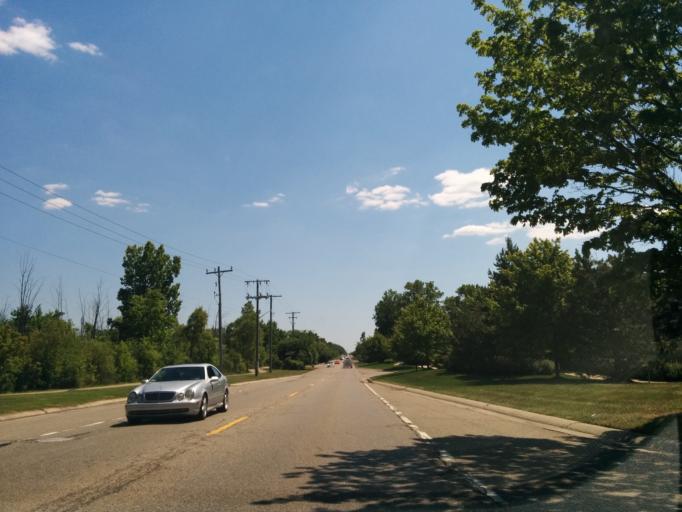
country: US
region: Michigan
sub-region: Oakland County
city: West Bloomfield Township
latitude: 42.5359
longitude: -83.3801
